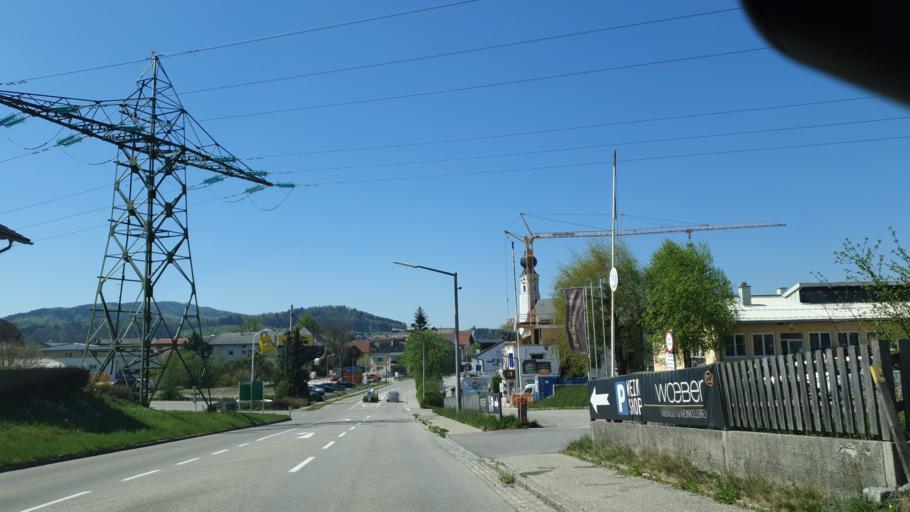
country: AT
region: Upper Austria
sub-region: Politischer Bezirk Vocklabruck
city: Sankt Georgen im Attergau
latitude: 47.9321
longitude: 13.4947
